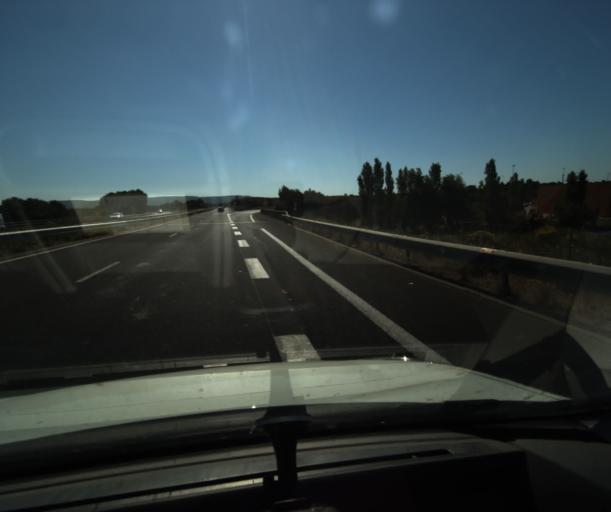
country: FR
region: Languedoc-Roussillon
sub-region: Departement de l'Aude
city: Narbonne
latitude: 43.1515
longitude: 2.9785
